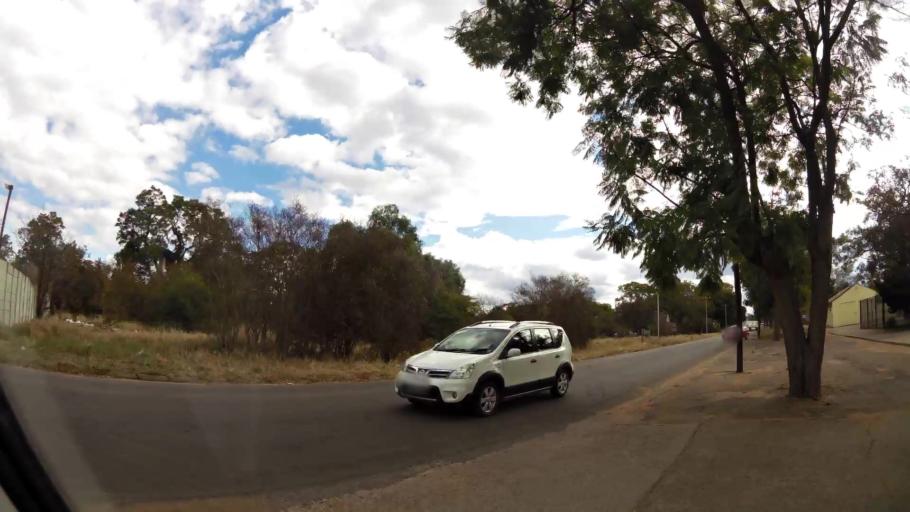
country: ZA
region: Limpopo
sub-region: Waterberg District Municipality
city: Modimolle
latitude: -24.7052
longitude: 28.4077
